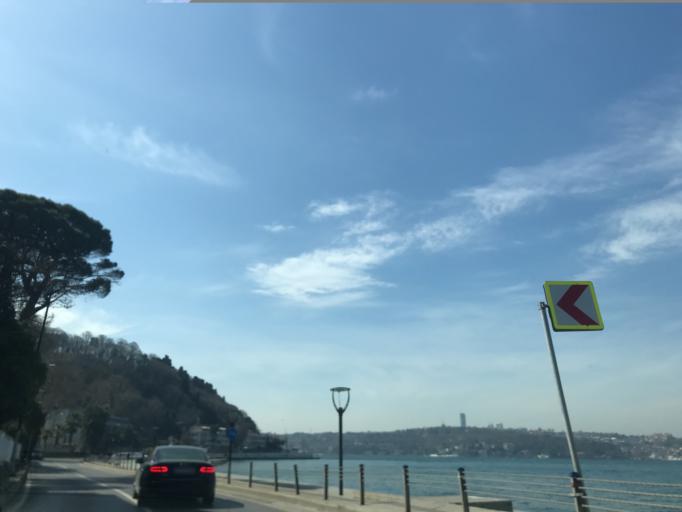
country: TR
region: Istanbul
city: Umraniye
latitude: 41.1073
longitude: 29.0826
